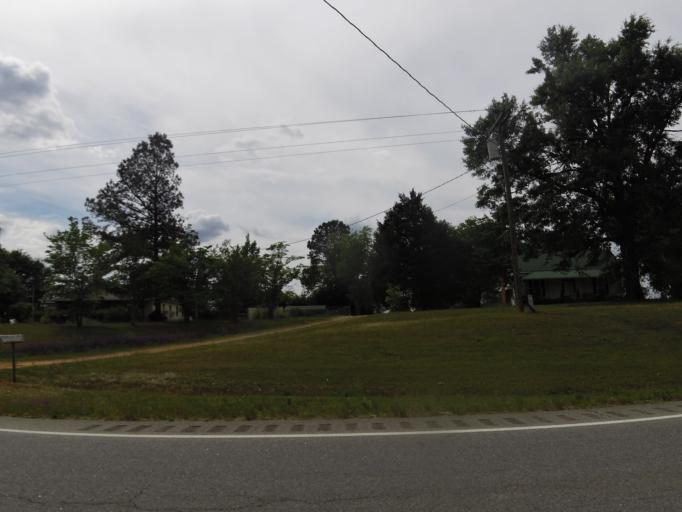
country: US
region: Georgia
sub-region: Jefferson County
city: Wrens
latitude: 33.1140
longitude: -82.4068
